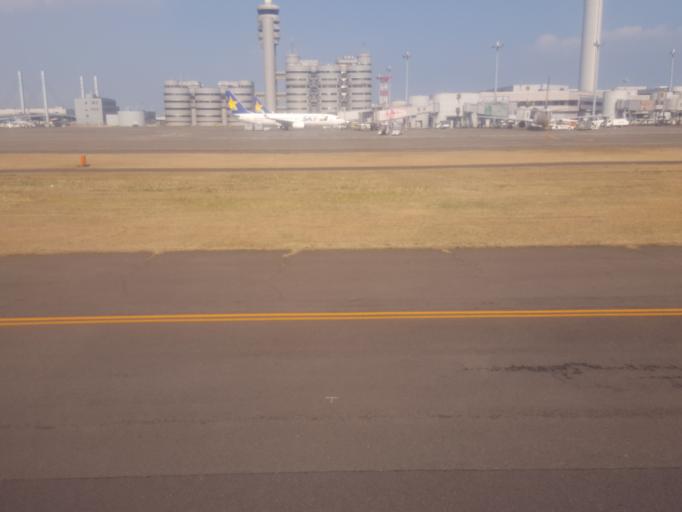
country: JP
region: Kanagawa
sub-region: Kawasaki-shi
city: Kawasaki
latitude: 35.5510
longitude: 139.7780
